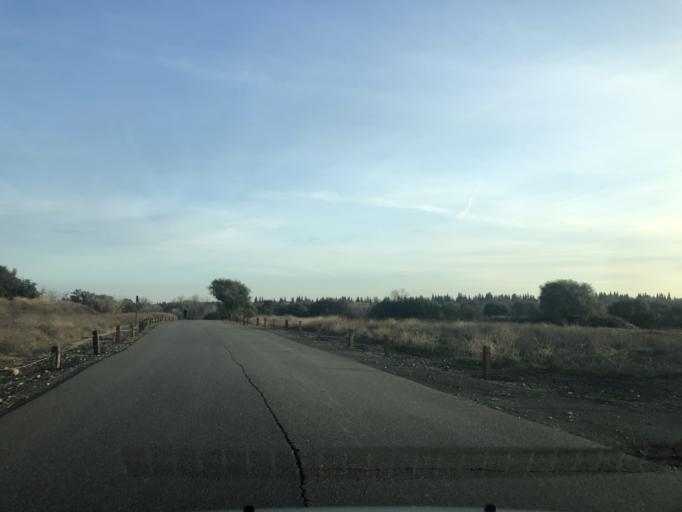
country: US
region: California
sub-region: Sacramento County
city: Gold River
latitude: 38.6375
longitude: -121.2367
